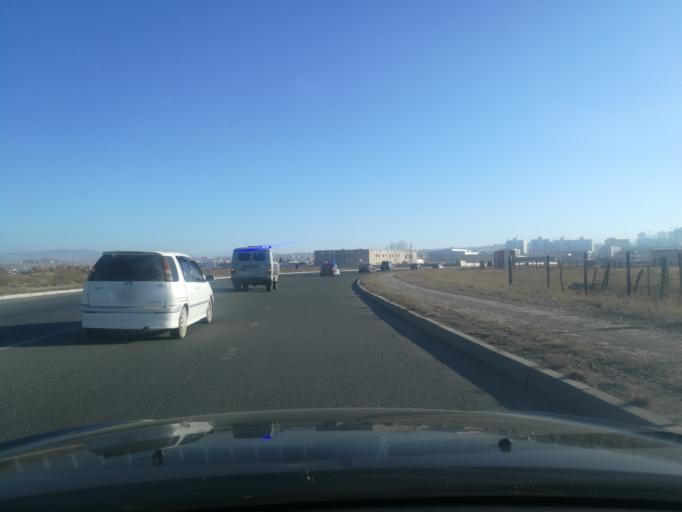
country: MN
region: Ulaanbaatar
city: Ulaanbaatar
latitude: 47.8564
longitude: 106.7493
